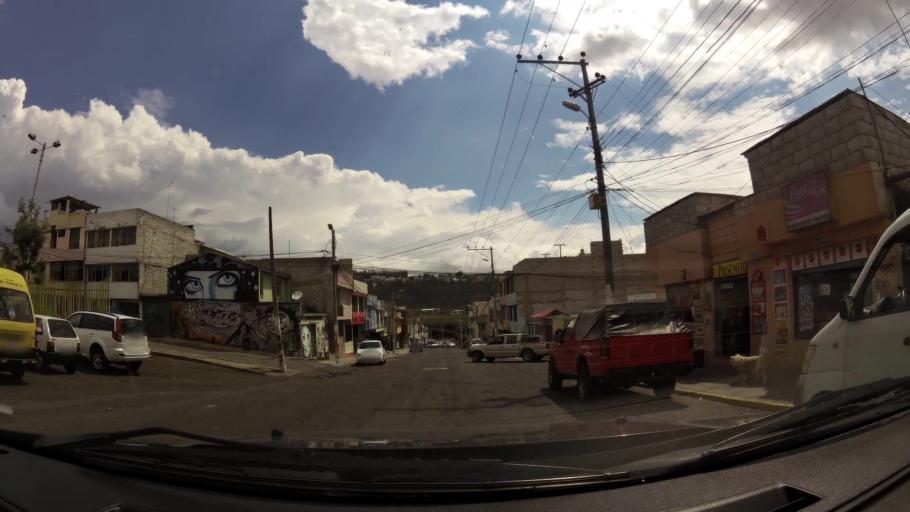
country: EC
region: Pichincha
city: Quito
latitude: -0.0893
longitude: -78.4523
